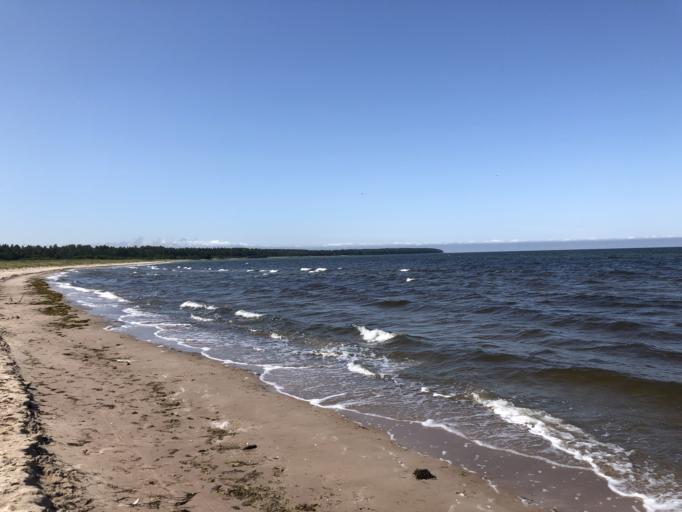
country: EE
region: Hiiumaa
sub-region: Kaerdla linn
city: Kardla
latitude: 58.9353
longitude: 22.3869
